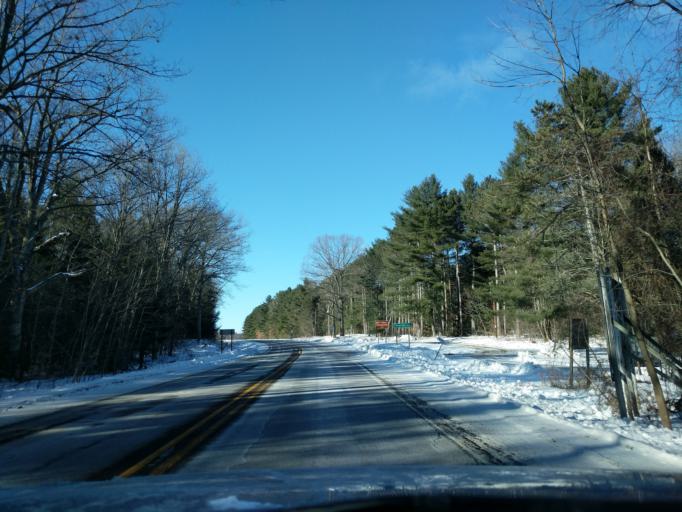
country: US
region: Wisconsin
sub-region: Menominee County
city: Keshena
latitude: 45.1171
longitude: -88.6566
